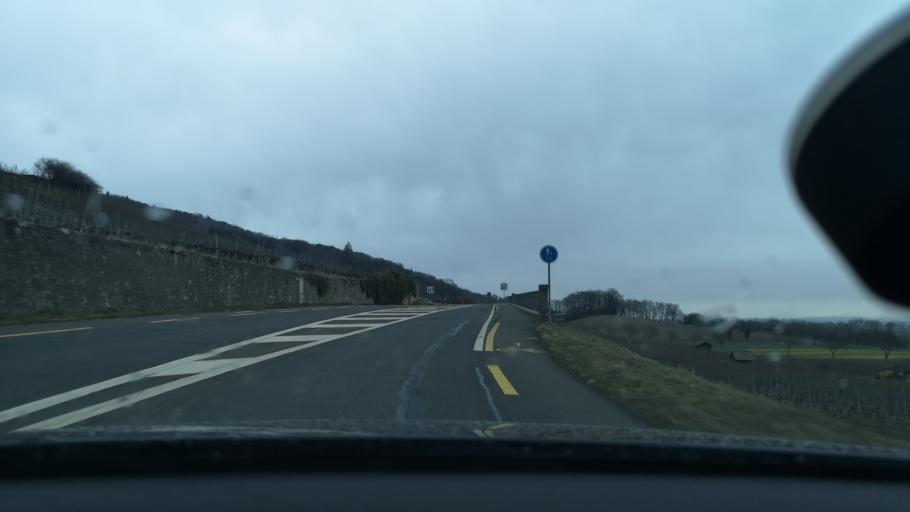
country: CH
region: Vaud
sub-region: Jura-Nord vaudois District
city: Yvonand
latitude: 46.8567
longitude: 6.7257
